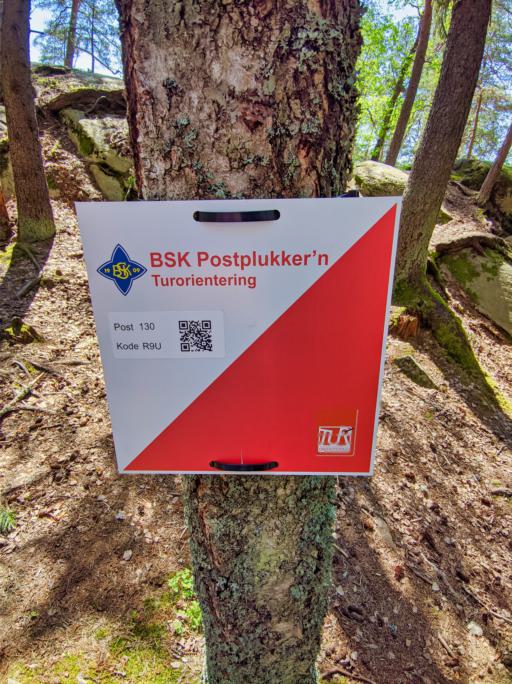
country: NO
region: Akershus
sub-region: Oppegard
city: Kolbotn
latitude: 59.8276
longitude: 10.7701
